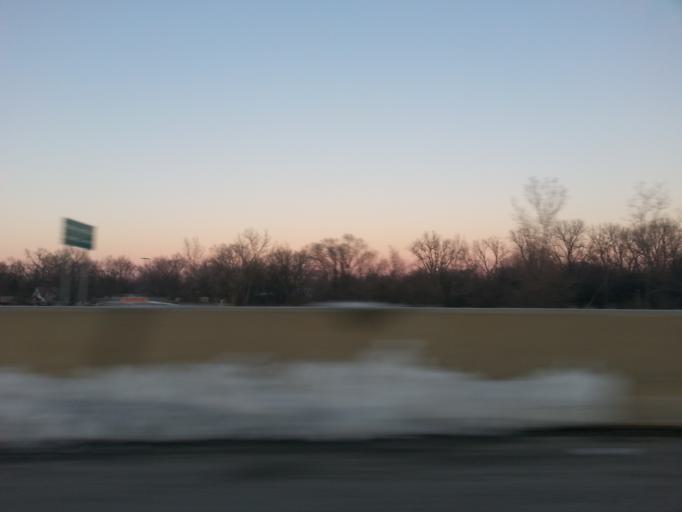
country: US
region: Illinois
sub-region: Cook County
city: Midlothian
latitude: 41.6376
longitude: -87.7173
